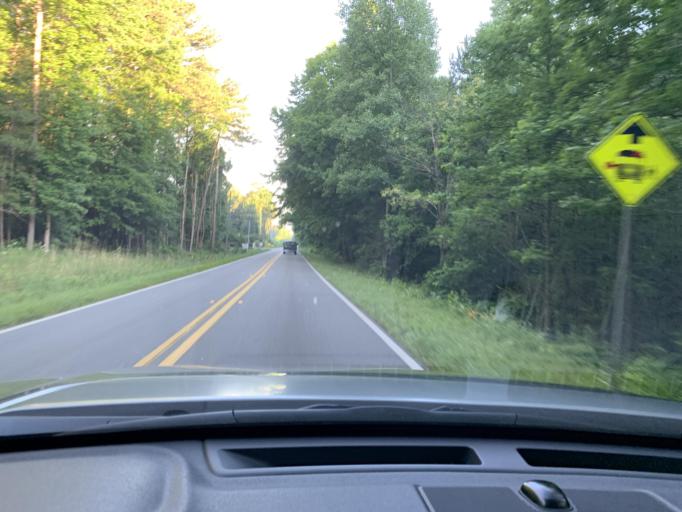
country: US
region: Georgia
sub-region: Bartow County
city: Rydal
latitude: 34.2746
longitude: -84.7346
